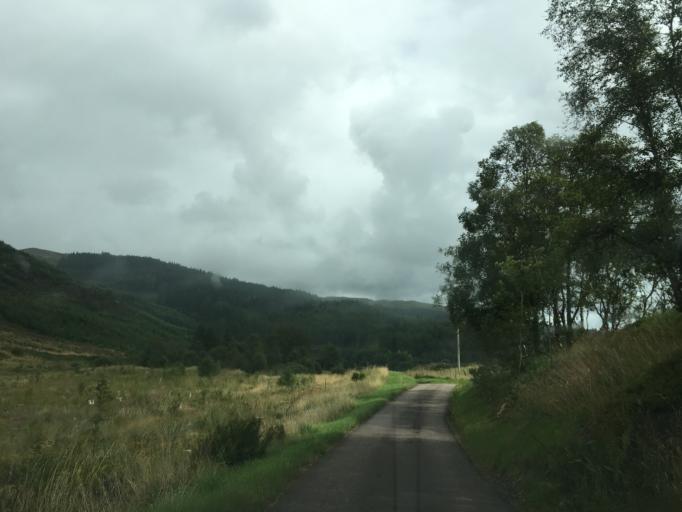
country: GB
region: Scotland
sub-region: Argyll and Bute
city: Oban
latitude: 56.2752
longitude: -5.3639
